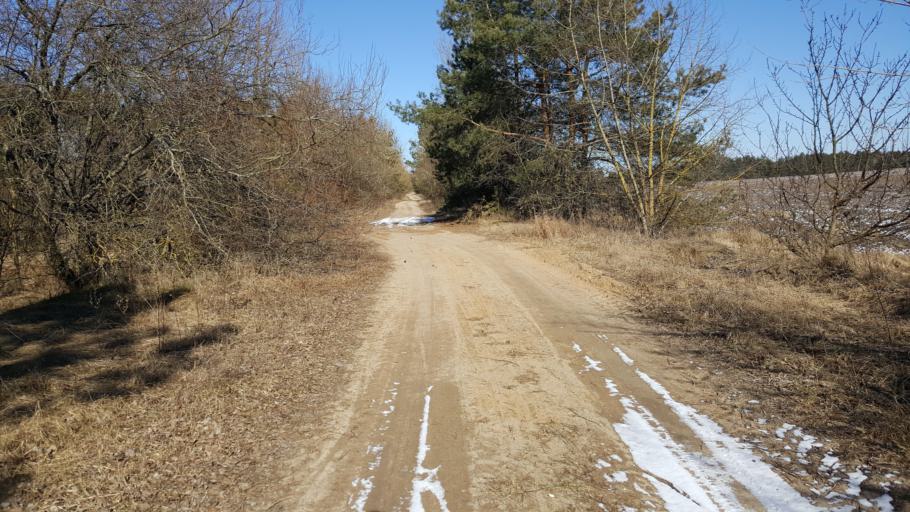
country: BY
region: Brest
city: Kamyanyets
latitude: 52.3826
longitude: 23.8430
